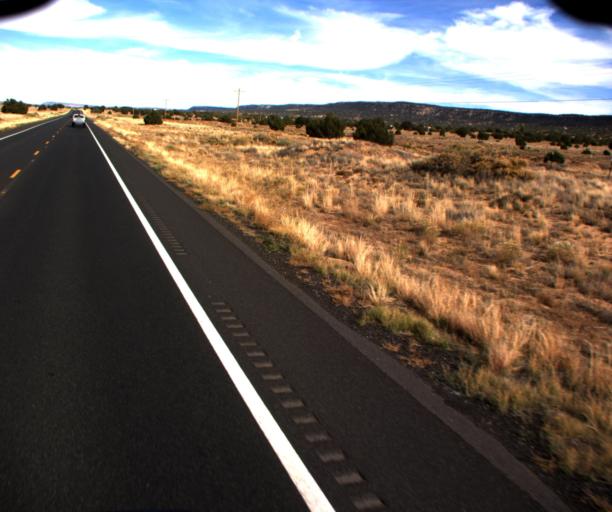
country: US
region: Arizona
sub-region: Coconino County
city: Kaibito
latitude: 36.4861
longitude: -110.6397
